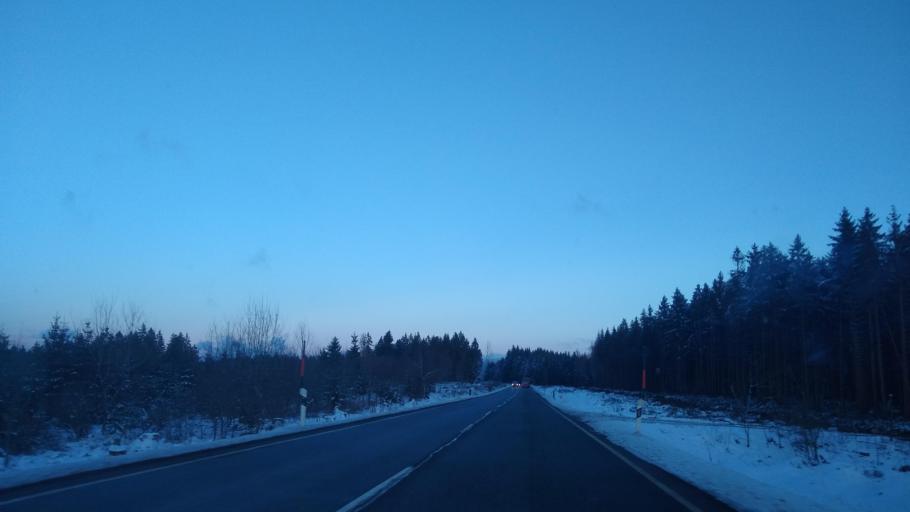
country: DE
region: Lower Saxony
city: Clausthal-Zellerfeld
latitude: 51.7901
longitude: 10.3818
